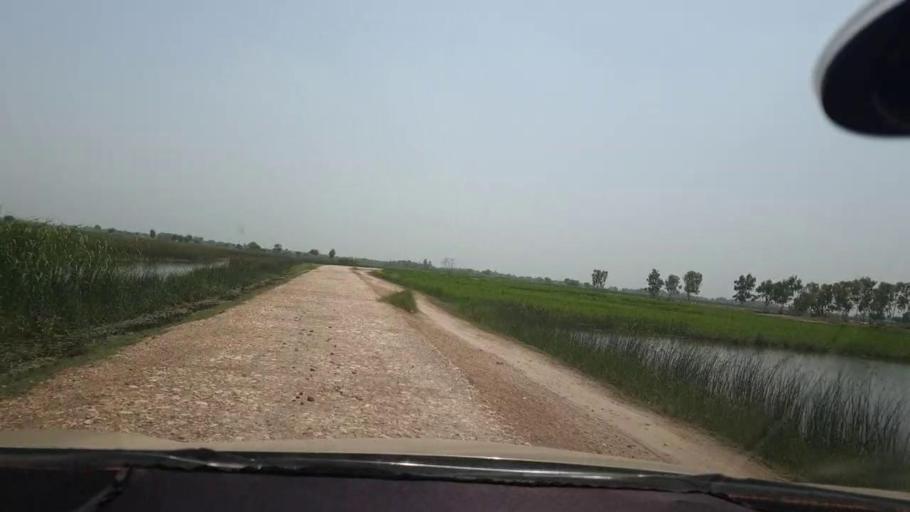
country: PK
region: Sindh
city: Kambar
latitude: 27.6516
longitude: 67.9321
